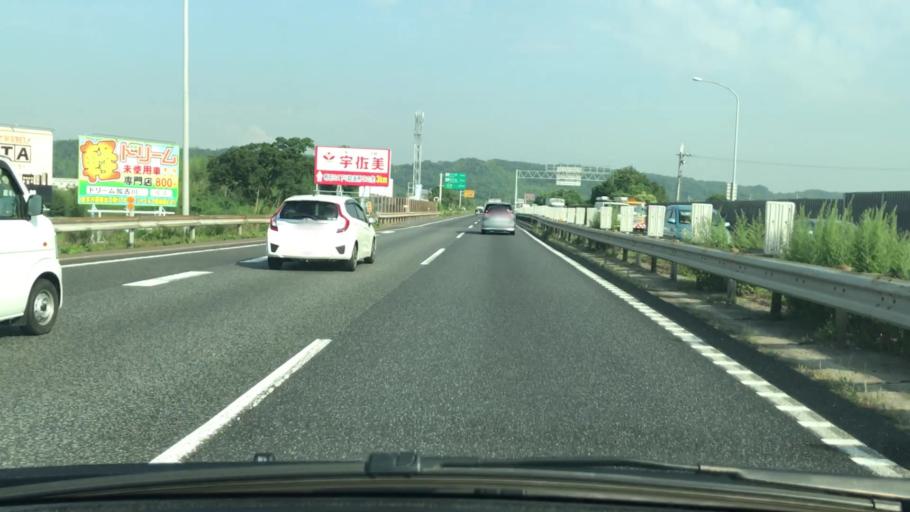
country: JP
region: Hyogo
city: Akashi
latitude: 34.6858
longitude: 134.9783
